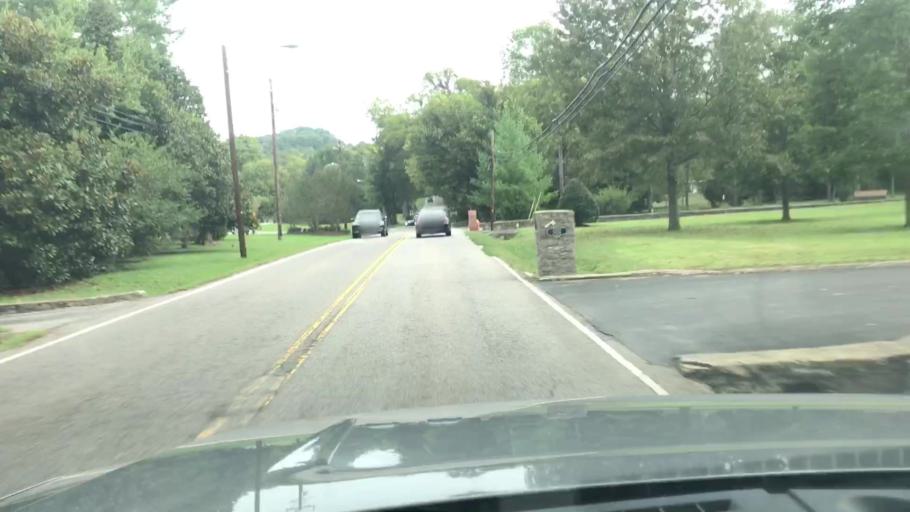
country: US
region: Tennessee
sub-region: Davidson County
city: Forest Hills
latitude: 36.0601
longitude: -86.8149
